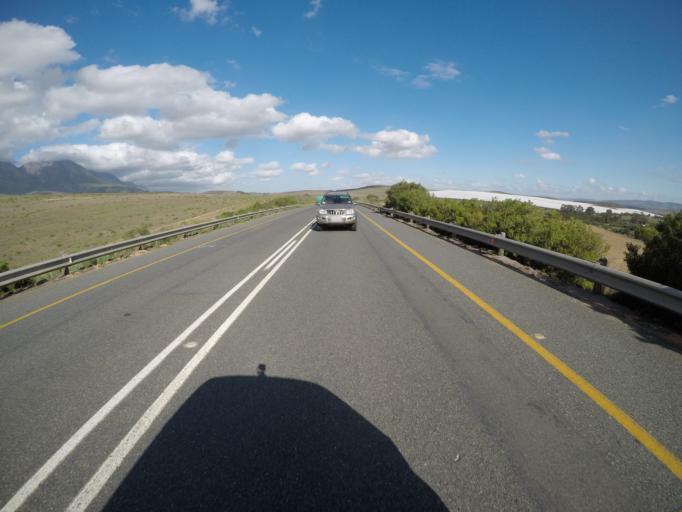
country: ZA
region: Western Cape
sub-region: Overberg District Municipality
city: Swellendam
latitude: -33.9574
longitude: 20.2366
